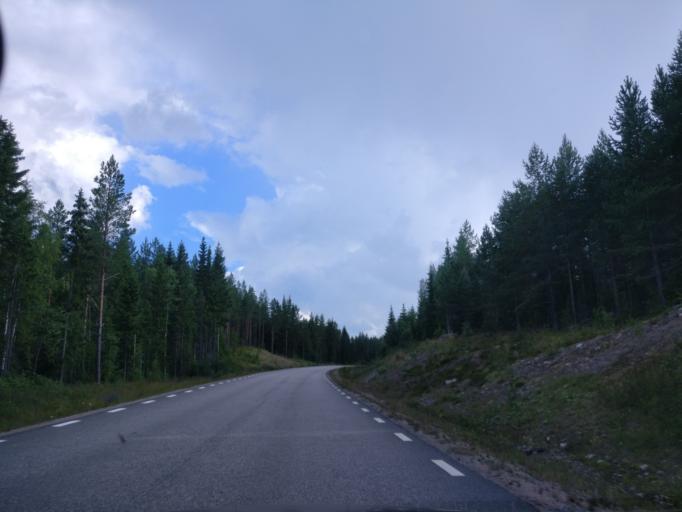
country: SE
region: Dalarna
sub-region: Ludvika Kommun
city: Abborrberget
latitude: 60.1780
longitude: 14.6731
